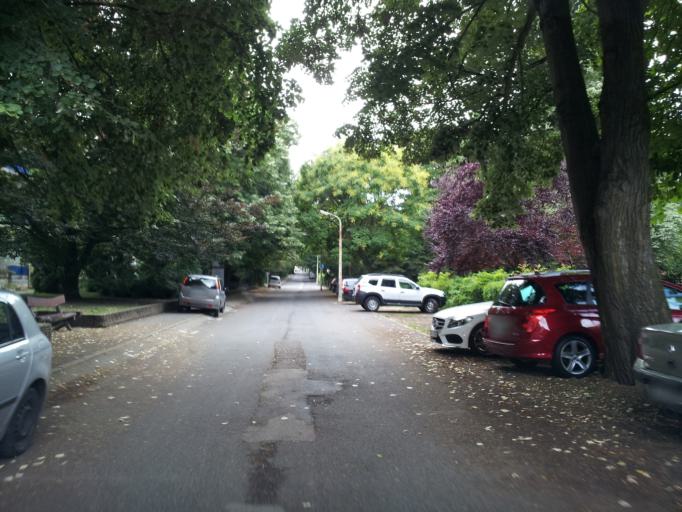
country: HU
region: Fejer
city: Lepseny
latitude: 46.9861
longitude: 18.1667
